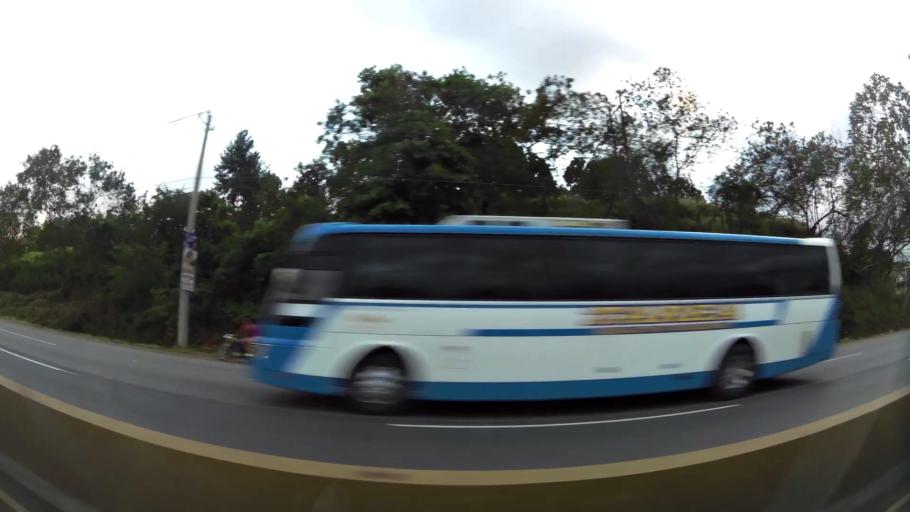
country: DO
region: Santo Domingo
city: Santo Domingo Oeste
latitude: 18.5614
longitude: -70.0645
